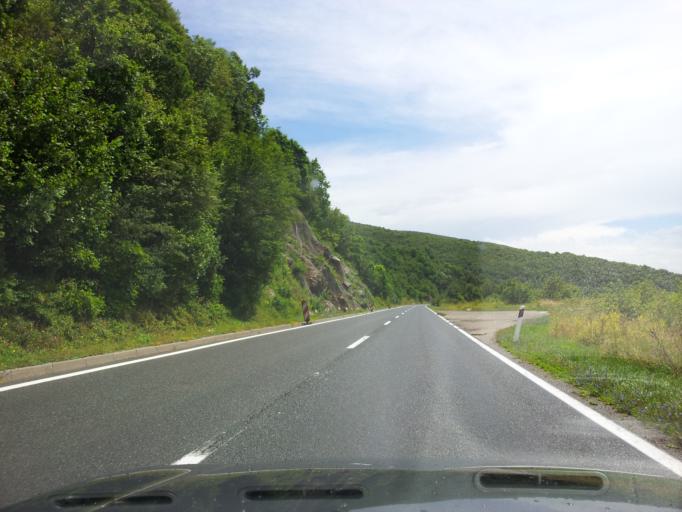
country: BA
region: Federation of Bosnia and Herzegovina
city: Bihac
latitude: 44.6163
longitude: 15.7388
